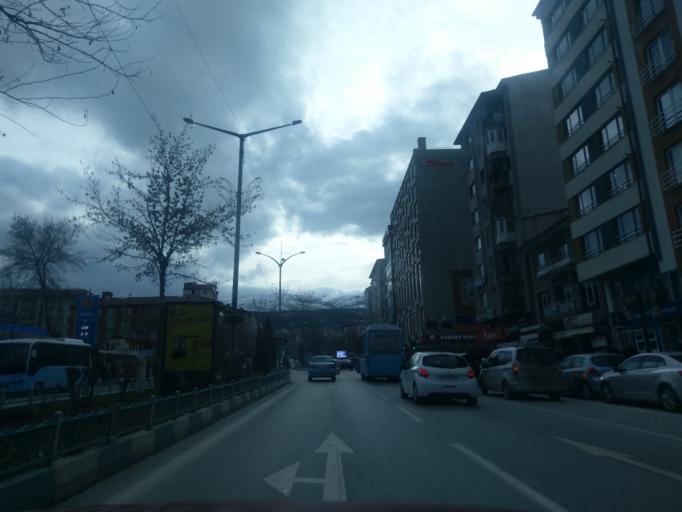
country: TR
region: Kuetahya
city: Kutahya
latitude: 39.4217
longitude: 29.9870
